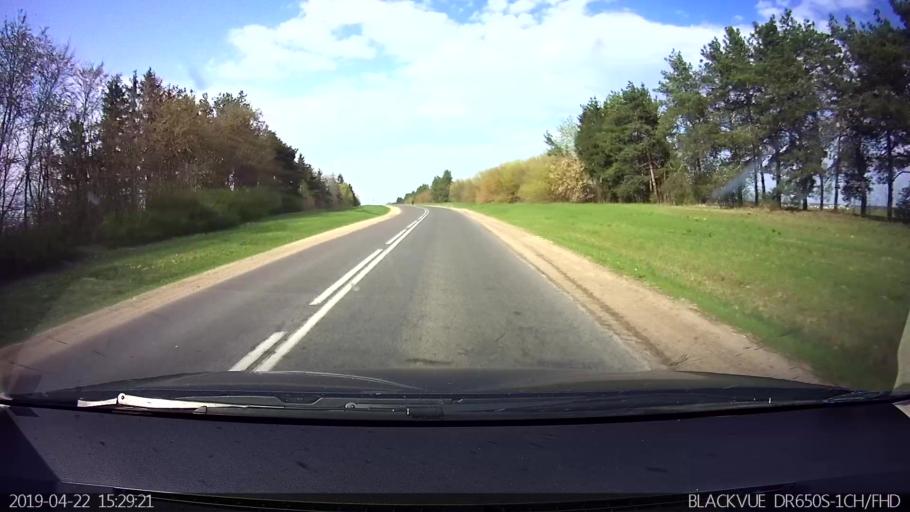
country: BY
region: Brest
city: Vysokaye
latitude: 52.3849
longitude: 23.3735
